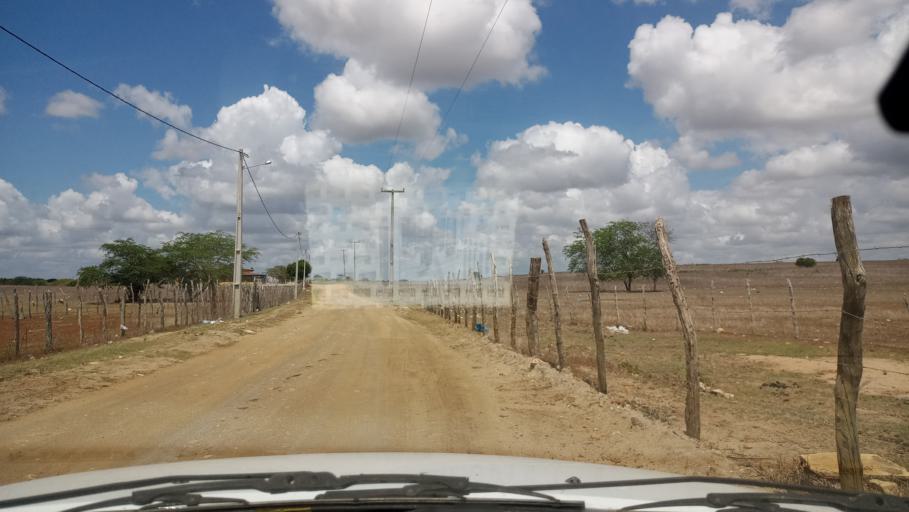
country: BR
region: Rio Grande do Norte
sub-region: Santo Antonio
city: Santo Antonio
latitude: -6.3472
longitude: -35.3779
